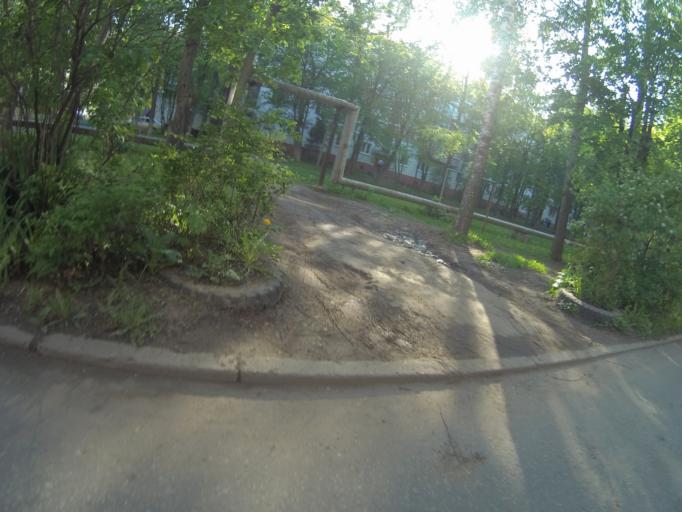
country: RU
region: Vladimir
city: Kommunar
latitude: 56.1686
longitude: 40.4626
